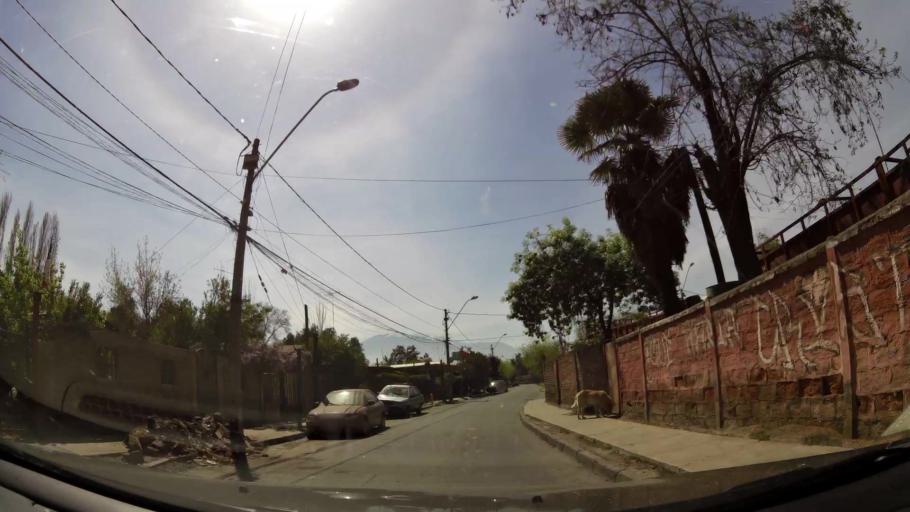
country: CL
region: Santiago Metropolitan
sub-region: Provincia de Cordillera
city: Puente Alto
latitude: -33.6260
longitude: -70.5771
